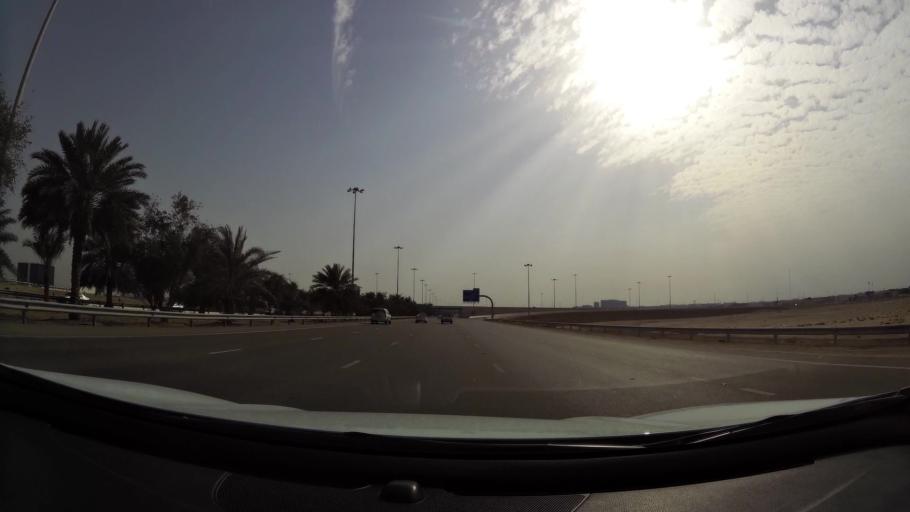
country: AE
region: Abu Dhabi
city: Abu Dhabi
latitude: 24.3432
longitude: 54.6384
